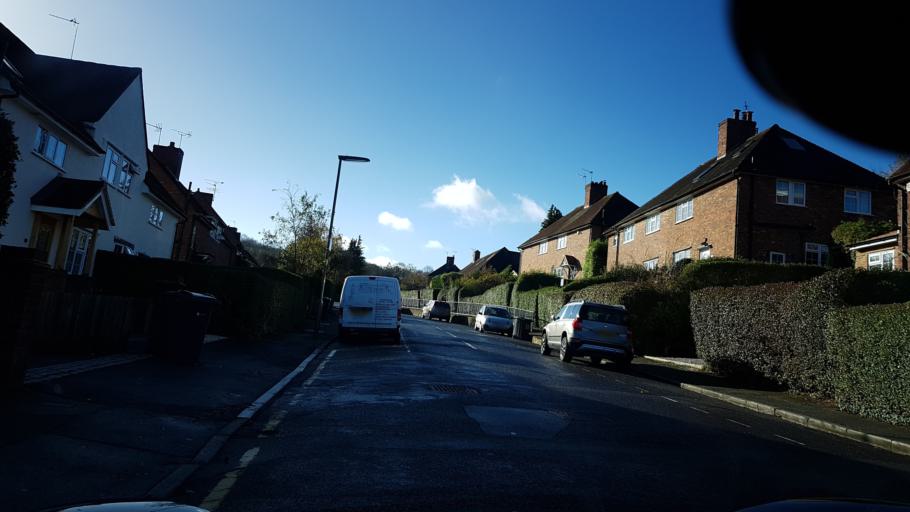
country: GB
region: England
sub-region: Surrey
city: Guildford
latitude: 51.2355
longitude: -0.5942
